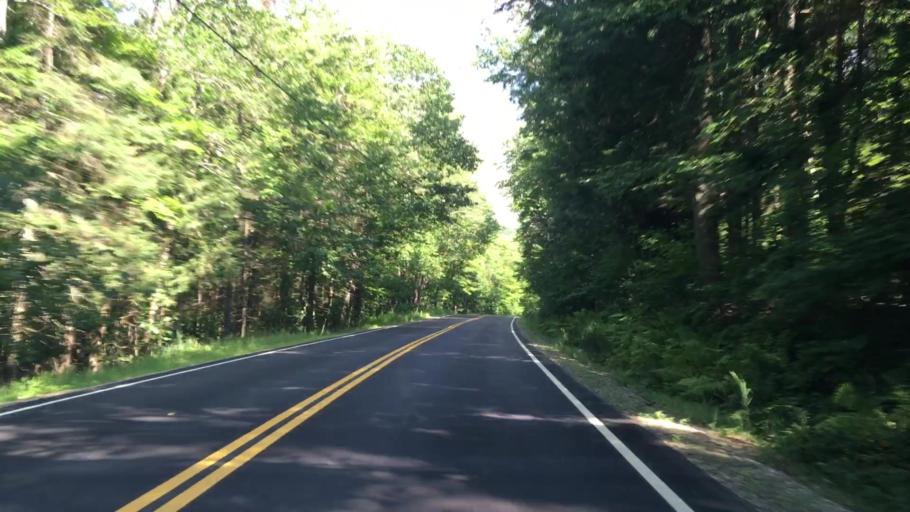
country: US
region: New Hampshire
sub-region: Grafton County
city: North Haverhill
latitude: 44.1151
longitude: -71.9086
